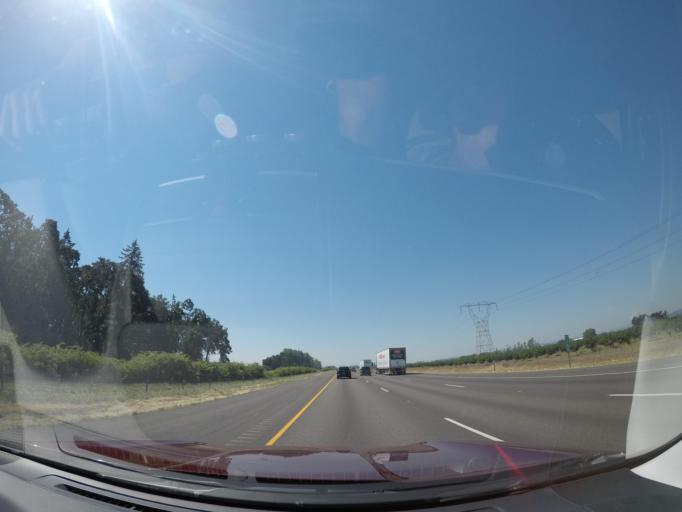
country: US
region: Oregon
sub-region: Marion County
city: Gervais
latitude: 45.0705
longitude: -122.9616
